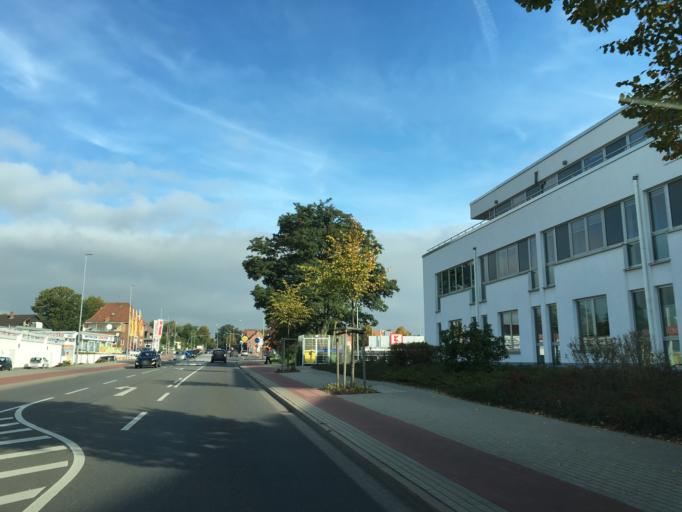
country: DE
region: Lower Saxony
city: Lueneburg
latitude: 53.2574
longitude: 10.4098
